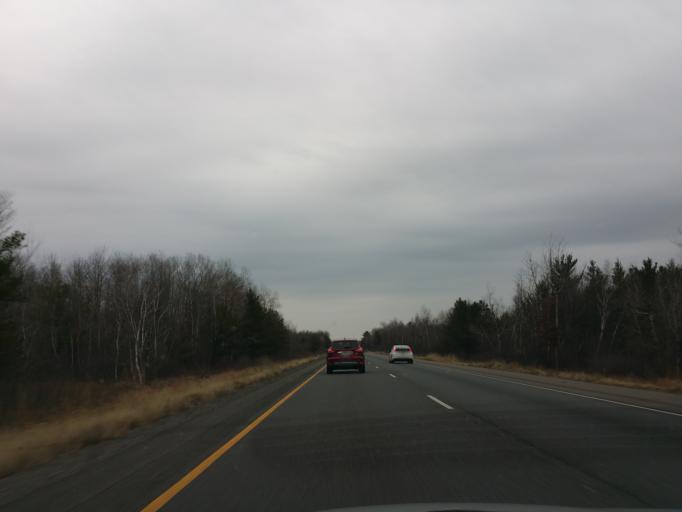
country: US
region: Wisconsin
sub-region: Jackson County
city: Black River Falls
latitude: 44.2626
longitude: -90.7732
